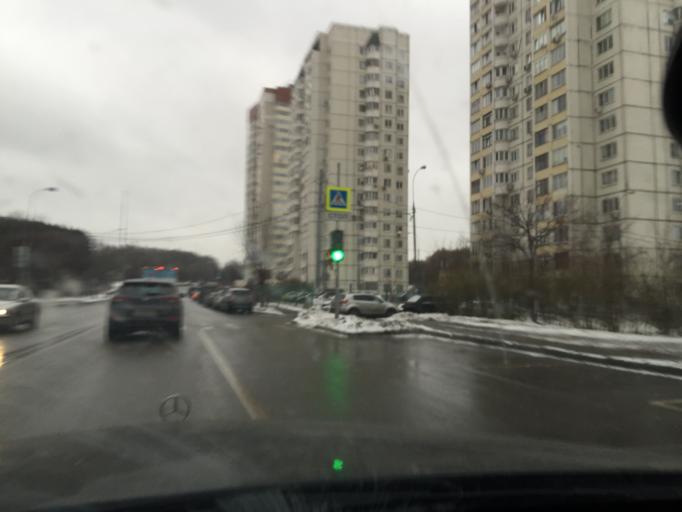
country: RU
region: Moscow
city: Troparevo
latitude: 55.6489
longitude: 37.4690
